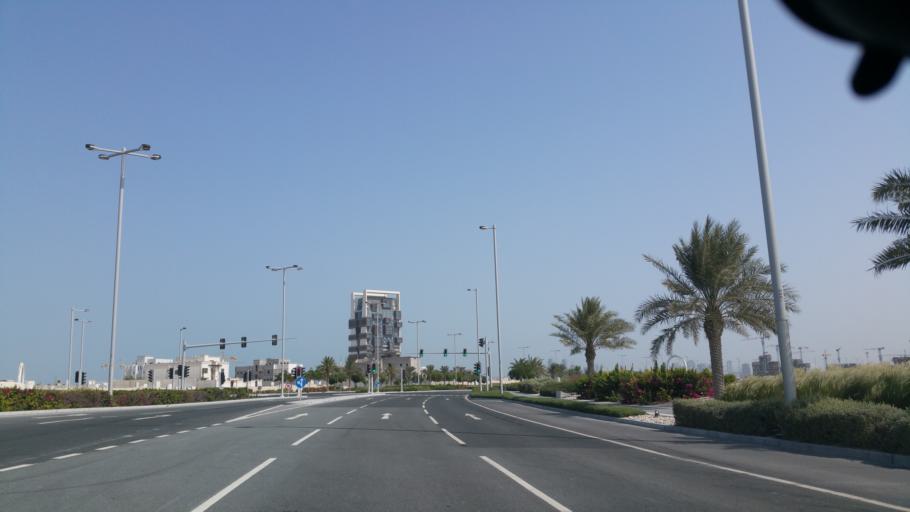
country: QA
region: Baladiyat Umm Salal
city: Umm Salal Muhammad
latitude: 25.4385
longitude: 51.5140
